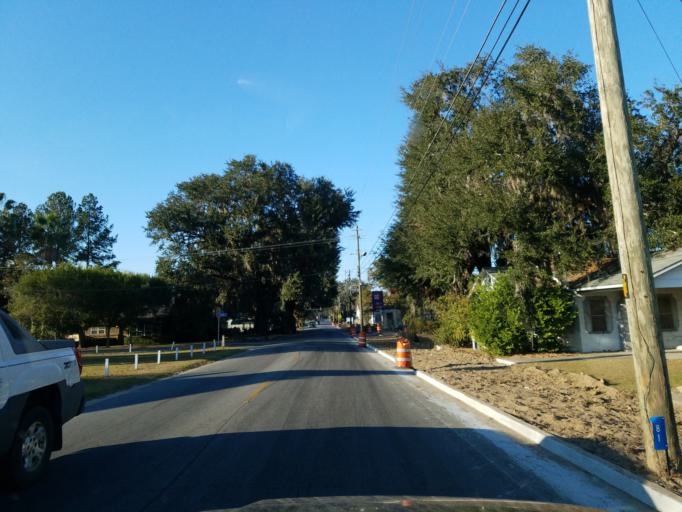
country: US
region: Georgia
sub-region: Lanier County
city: Lakeland
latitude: 31.0357
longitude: -83.0695
